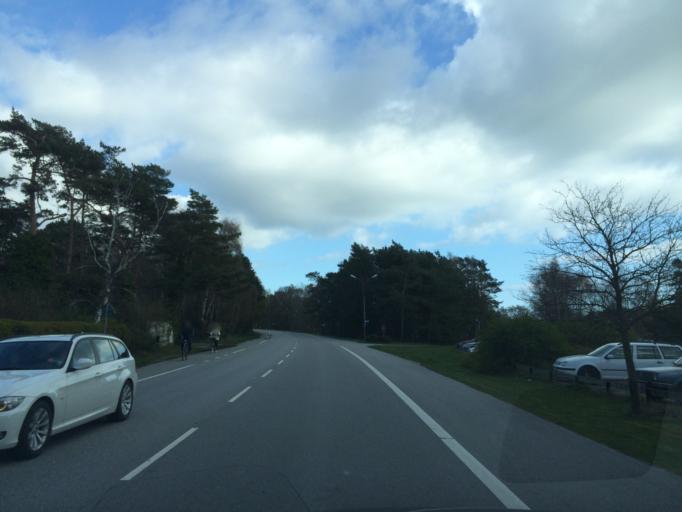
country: SE
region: Skane
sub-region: Vellinge Kommun
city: Skanor med Falsterbo
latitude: 55.4086
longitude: 12.8443
